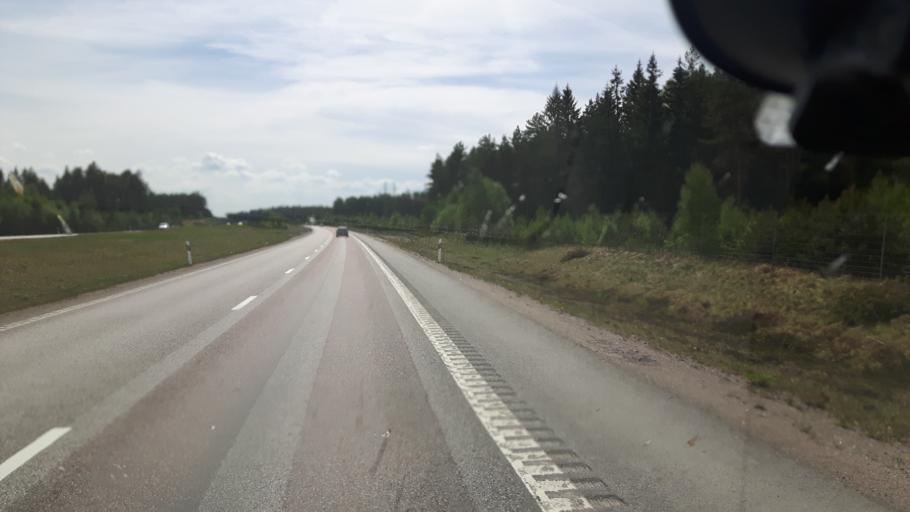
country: SE
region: Uppsala
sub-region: Tierps Kommun
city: Tierp
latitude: 60.2917
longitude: 17.5102
